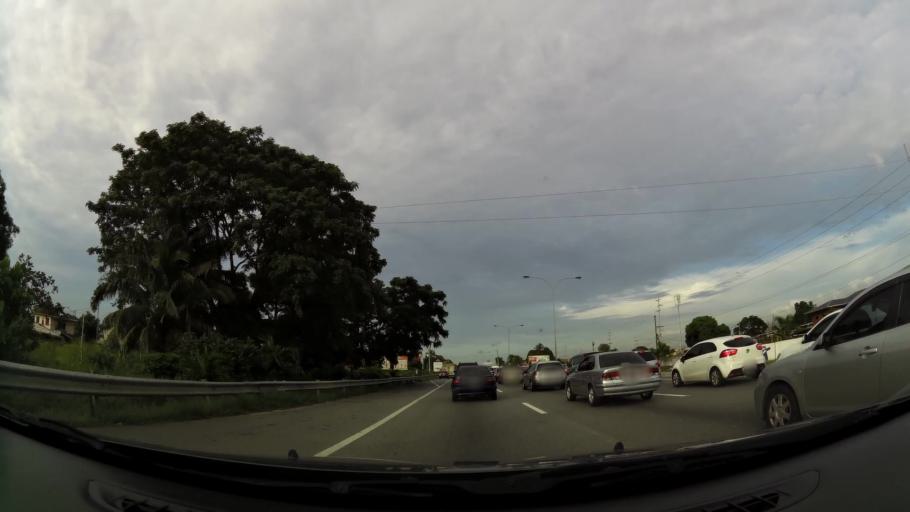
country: TT
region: Tunapuna/Piarco
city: Tunapuna
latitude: 10.6370
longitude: -61.3926
